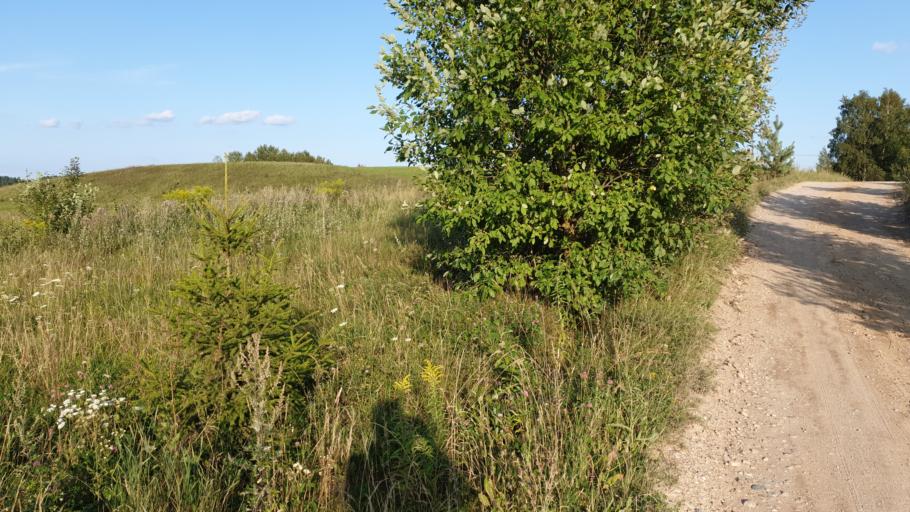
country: LT
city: Grigiskes
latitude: 54.7688
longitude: 25.0277
